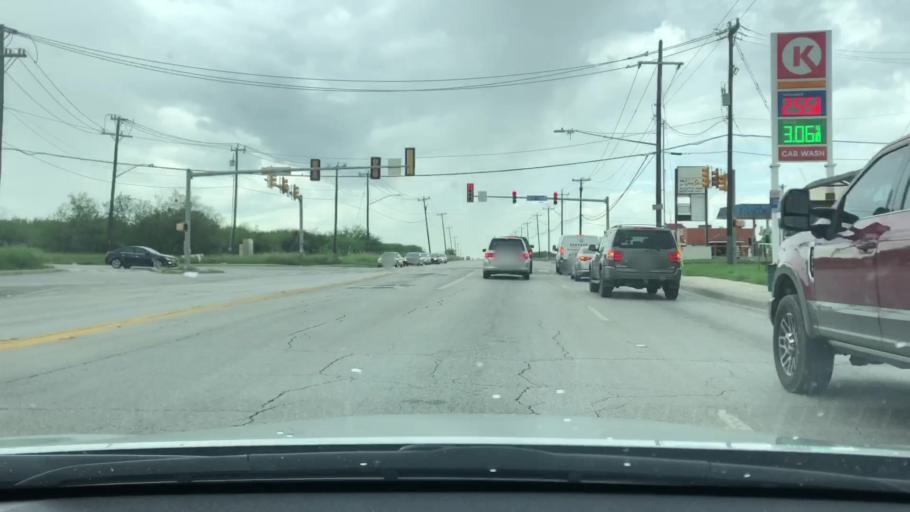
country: US
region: Texas
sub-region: Bexar County
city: Kirby
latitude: 29.4841
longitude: -98.3712
